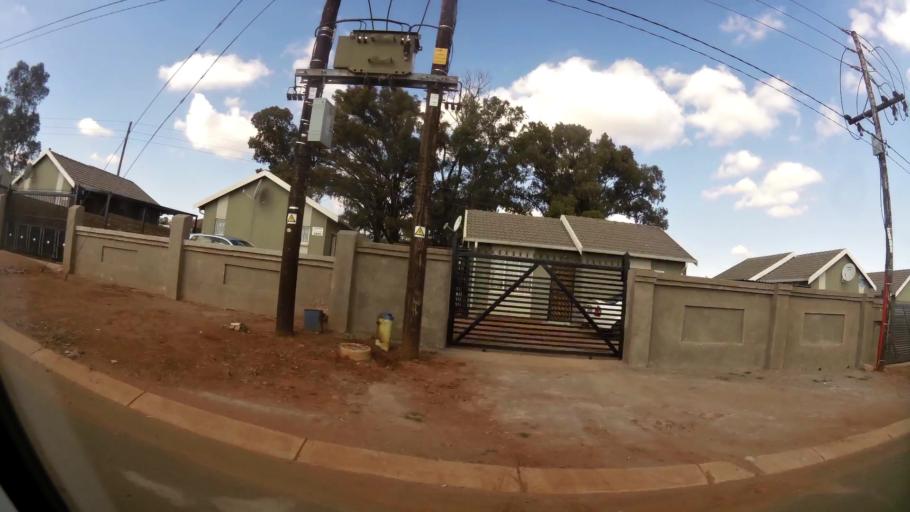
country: ZA
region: Gauteng
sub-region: City of Tshwane Metropolitan Municipality
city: Cullinan
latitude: -25.6904
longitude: 28.4070
